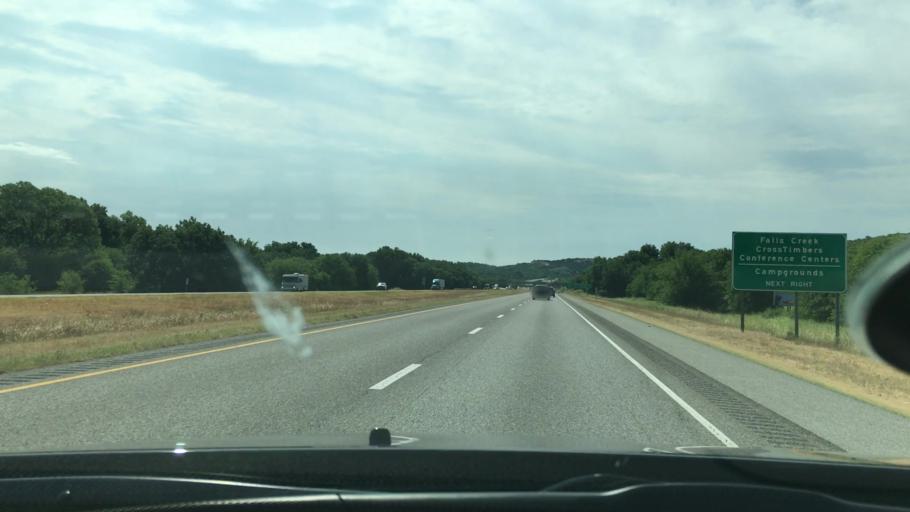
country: US
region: Oklahoma
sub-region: Murray County
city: Davis
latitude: 34.4608
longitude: -97.1454
